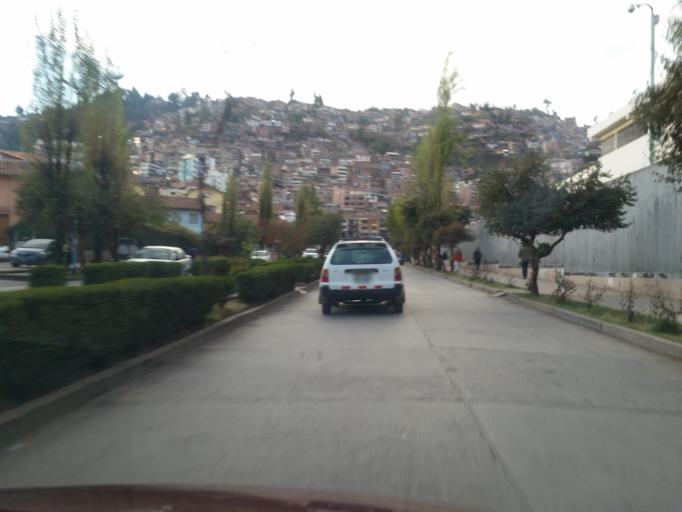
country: PE
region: Cusco
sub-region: Provincia de Cusco
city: Cusco
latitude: -13.5223
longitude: -71.9611
